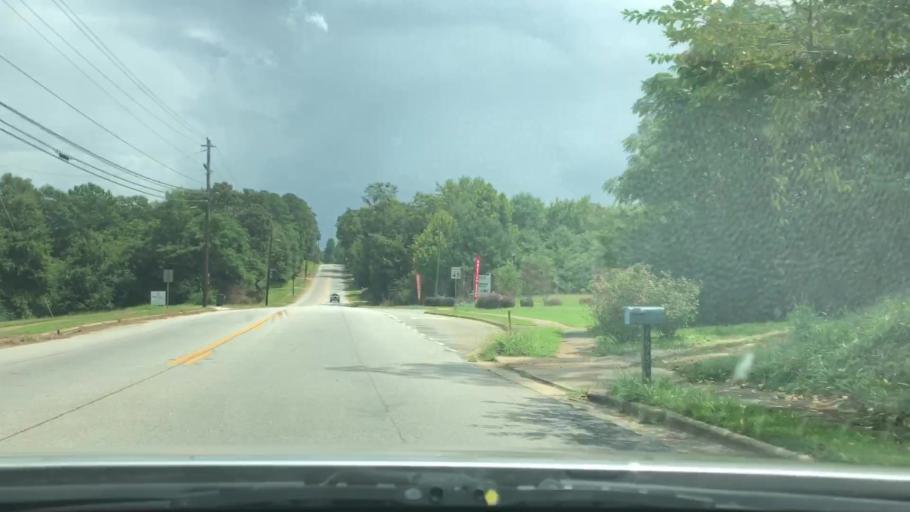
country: US
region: Georgia
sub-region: Pike County
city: Zebulon
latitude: 33.1020
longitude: -84.3395
